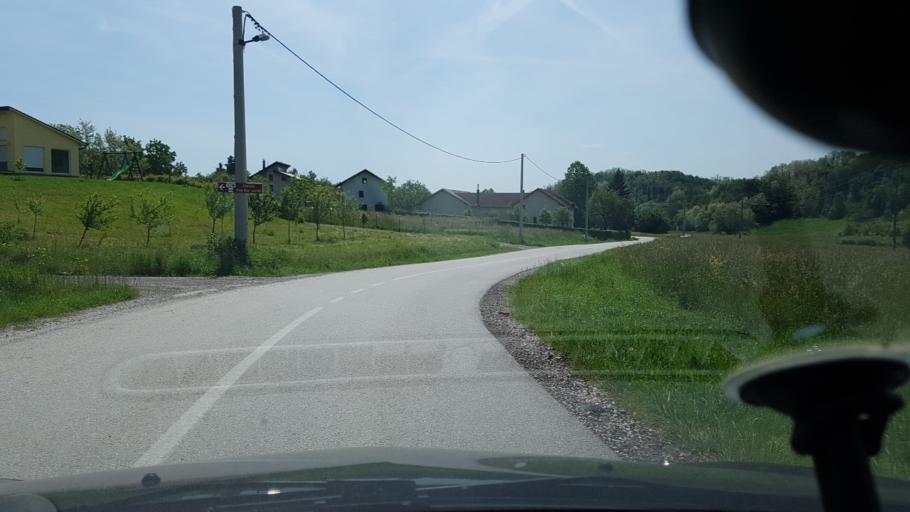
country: HR
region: Krapinsko-Zagorska
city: Marija Bistrica
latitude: 45.9360
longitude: 16.2074
